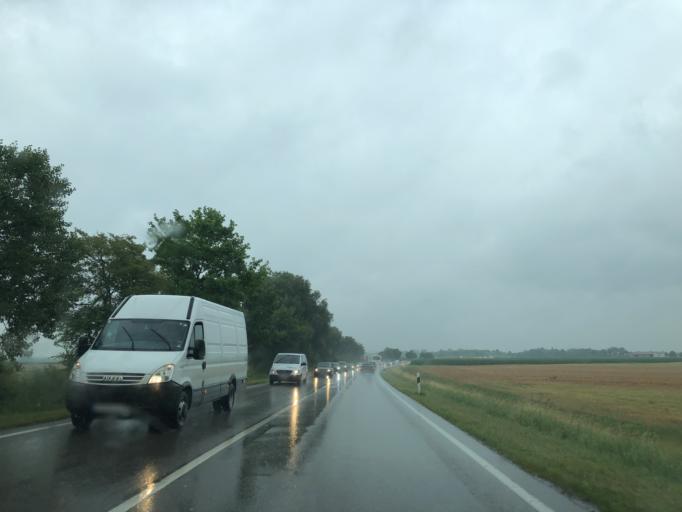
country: DE
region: Bavaria
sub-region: Upper Bavaria
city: Oberding
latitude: 48.3291
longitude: 11.8776
